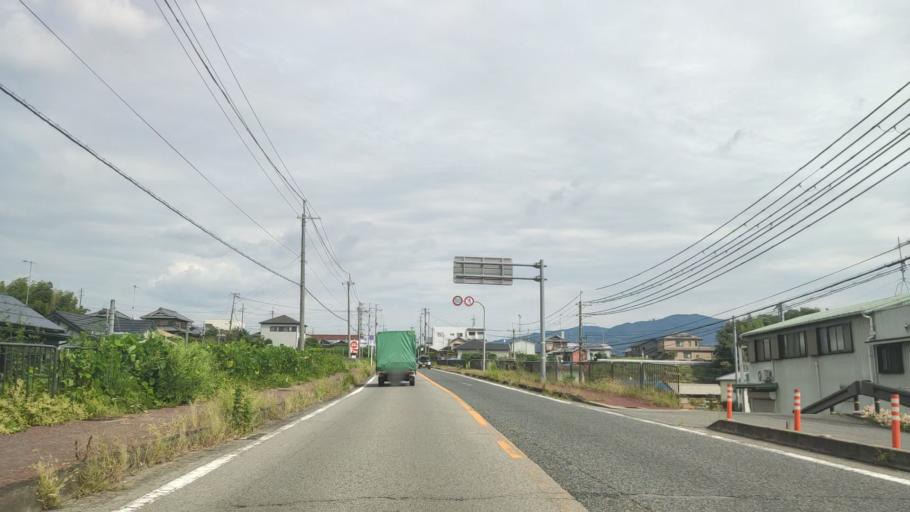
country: JP
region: Wakayama
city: Hashimoto
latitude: 34.3029
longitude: 135.5605
